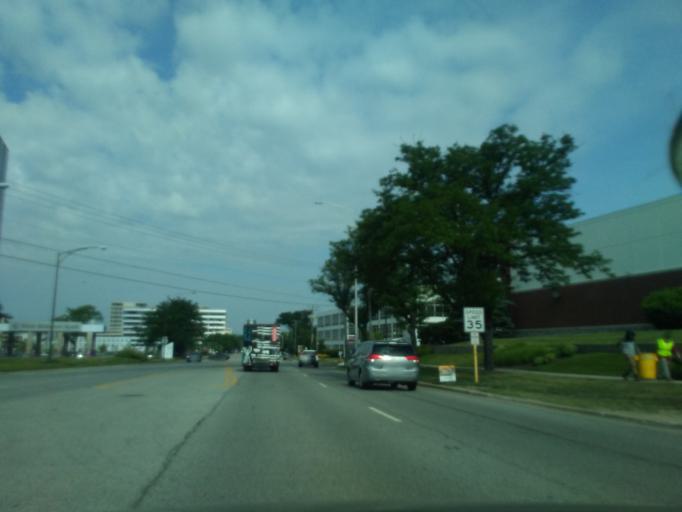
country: US
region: Illinois
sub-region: Cook County
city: Park Ridge
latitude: 41.9866
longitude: -87.8377
